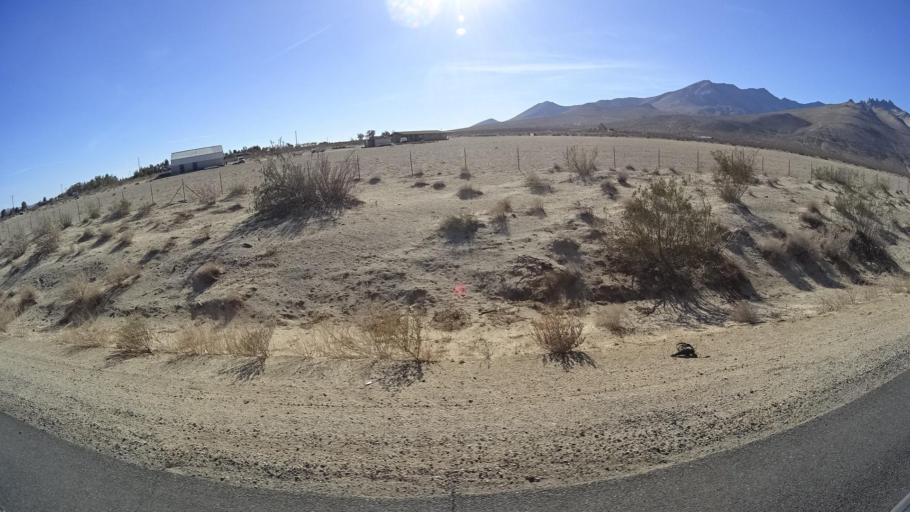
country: US
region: California
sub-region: Kern County
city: Inyokern
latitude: 35.6868
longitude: -117.8529
